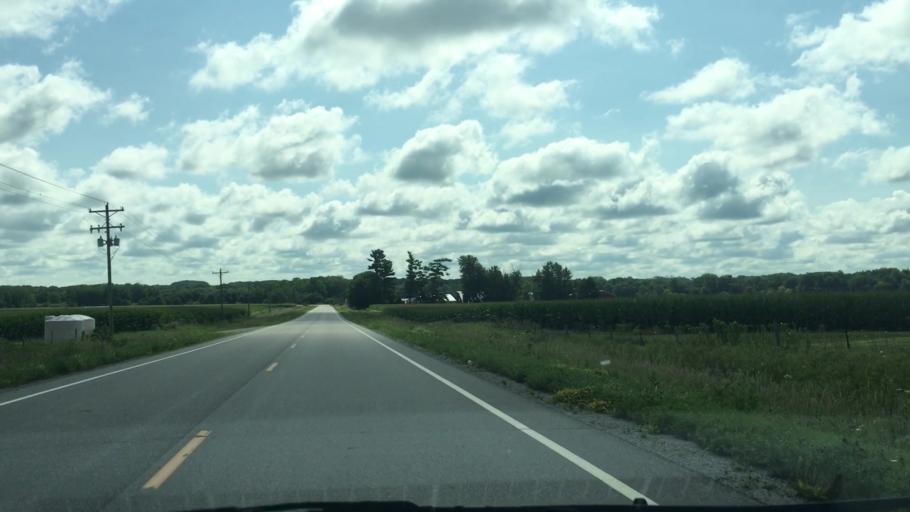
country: US
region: Iowa
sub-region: Linn County
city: Mount Vernon
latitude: 41.8417
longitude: -91.4073
